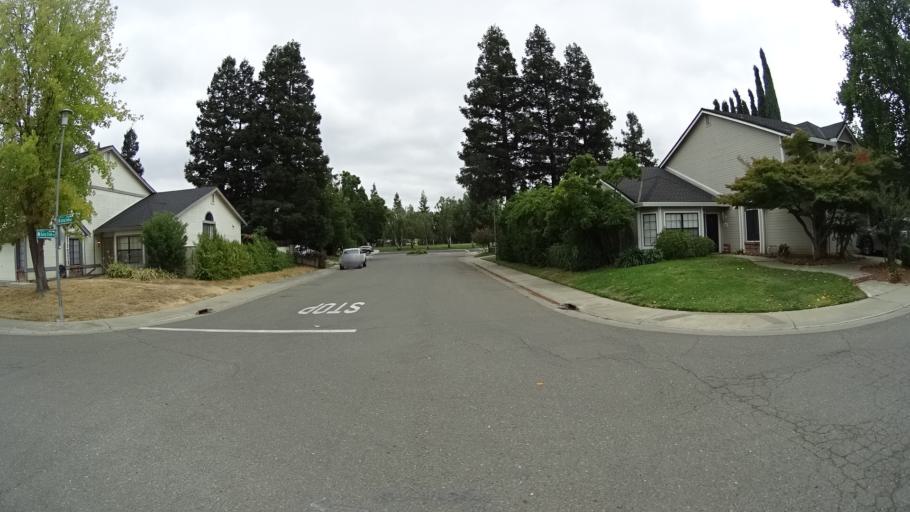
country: US
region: California
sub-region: Sacramento County
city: Laguna
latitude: 38.4214
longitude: -121.4414
